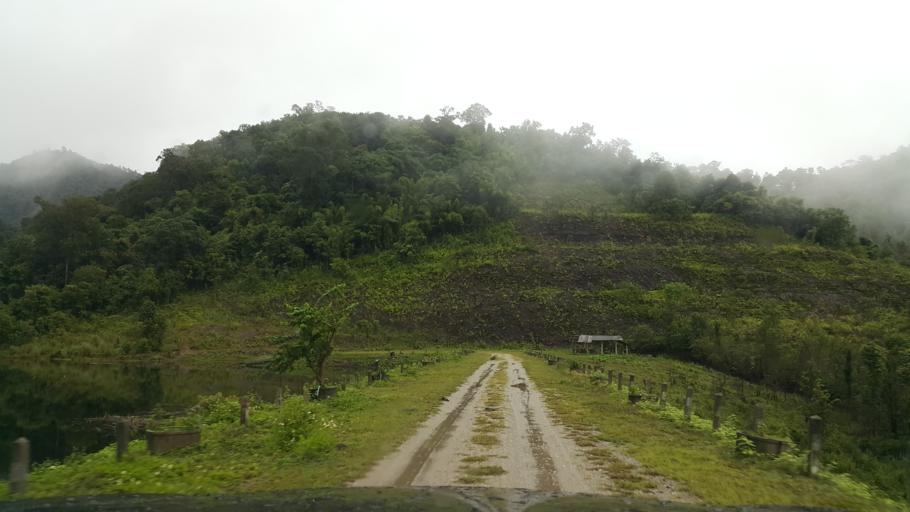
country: TH
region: Phayao
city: Phu Sang
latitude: 19.6001
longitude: 100.4120
